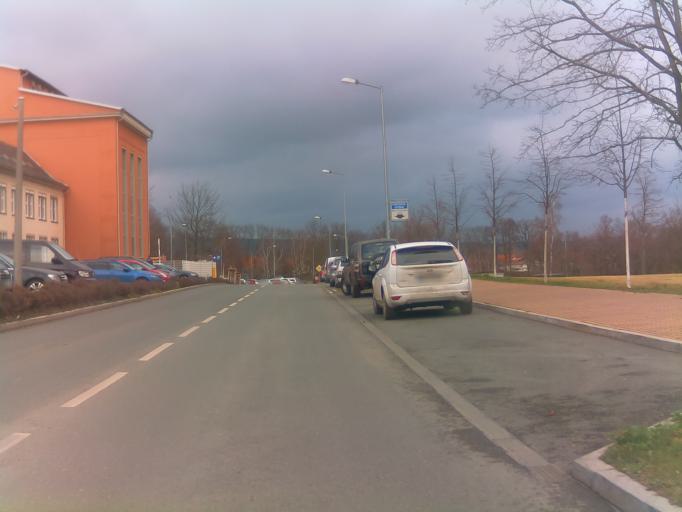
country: DE
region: Thuringia
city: Saalfeld
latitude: 50.6452
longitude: 11.3455
